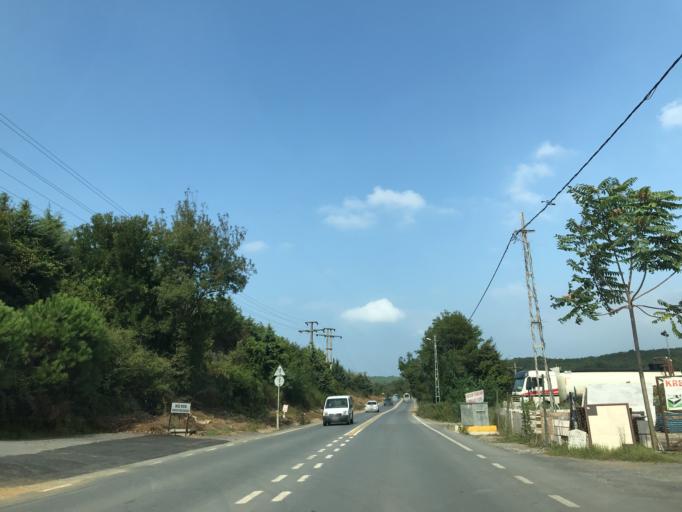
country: TR
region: Istanbul
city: Arikoey
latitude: 41.2268
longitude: 29.0366
